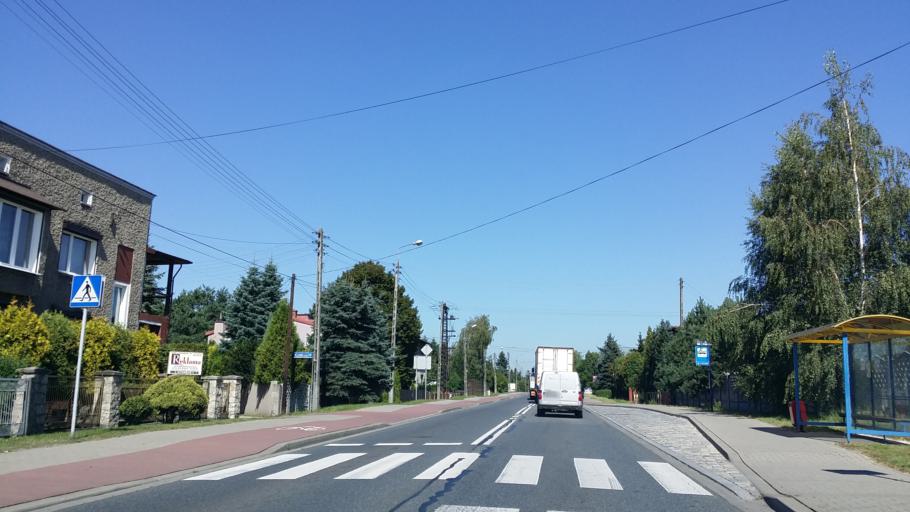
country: PL
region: Silesian Voivodeship
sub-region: Powiat bierunsko-ledzinski
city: Imielin
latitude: 50.1528
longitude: 19.1809
